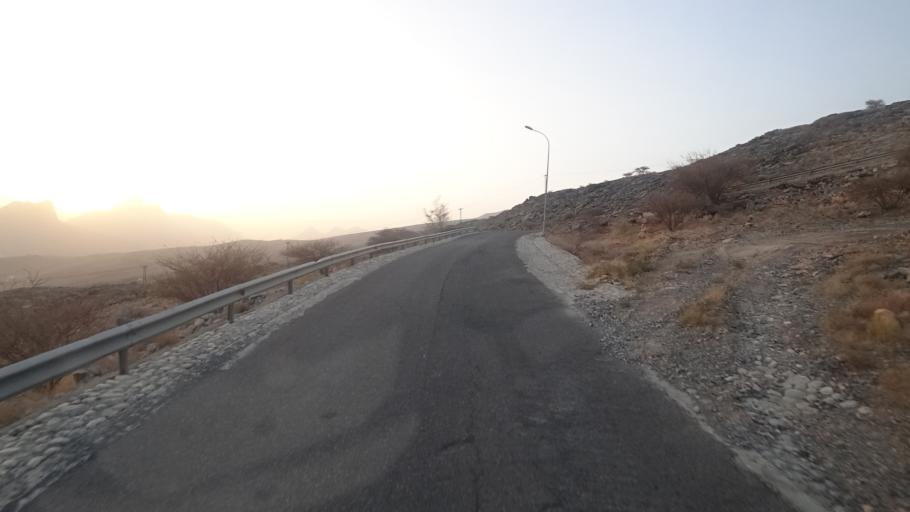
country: OM
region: Muhafazat ad Dakhiliyah
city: Bahla'
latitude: 23.1310
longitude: 57.3037
